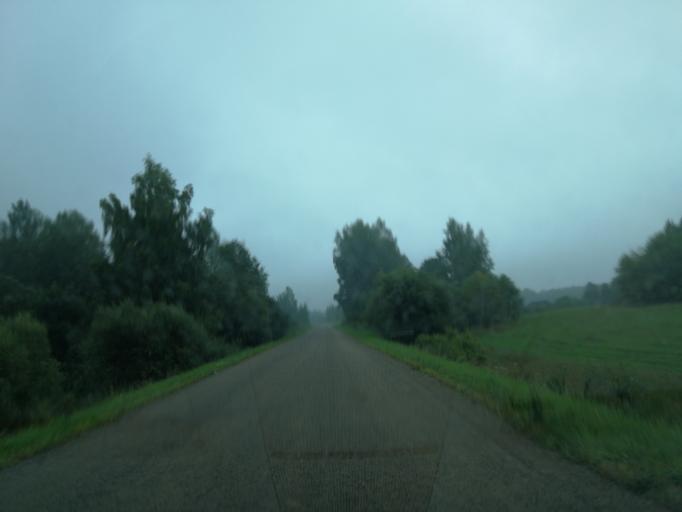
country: LV
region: Preilu Rajons
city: Jaunaglona
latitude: 56.3050
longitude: 26.9960
